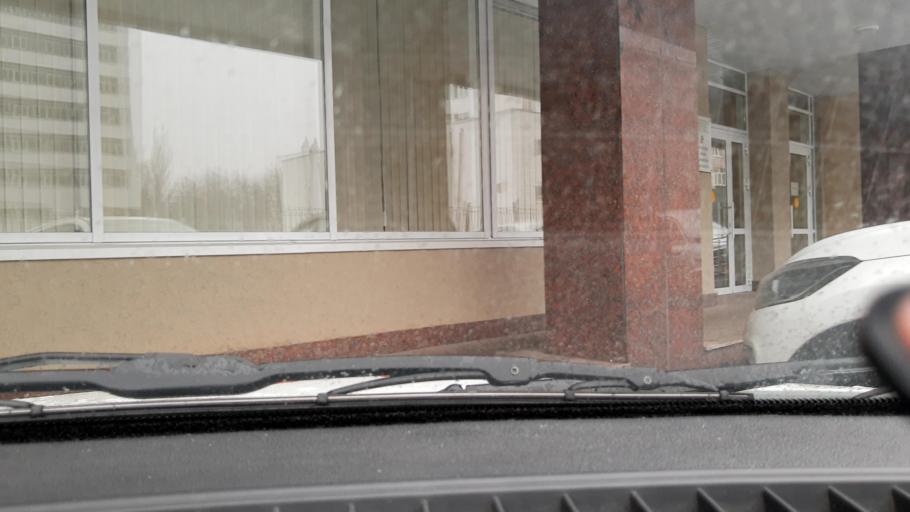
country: RU
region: Bashkortostan
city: Ufa
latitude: 54.7629
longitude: 56.0112
